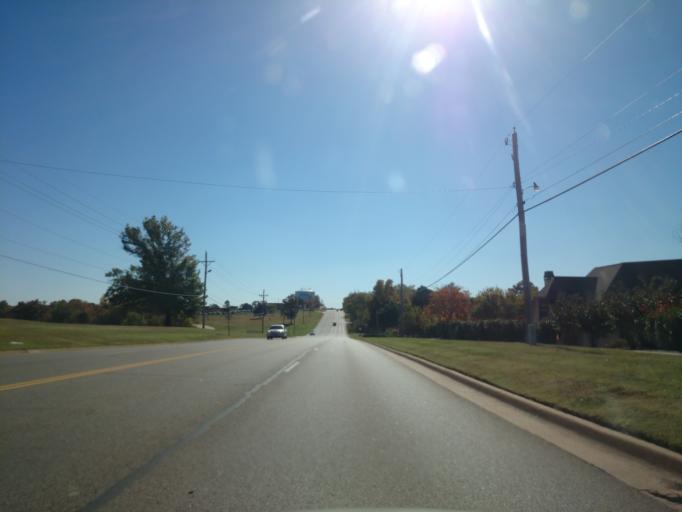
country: US
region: Oklahoma
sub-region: Payne County
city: Stillwater
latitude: 36.1544
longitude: -97.0697
